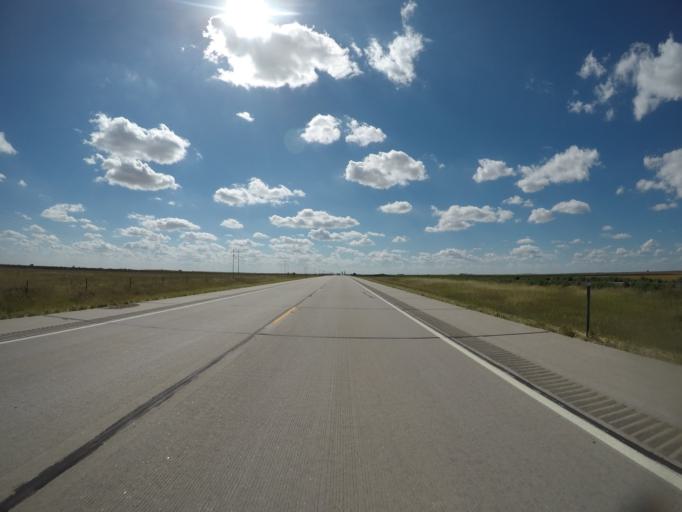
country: US
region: Colorado
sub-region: Phillips County
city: Holyoke
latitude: 40.6028
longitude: -102.4142
